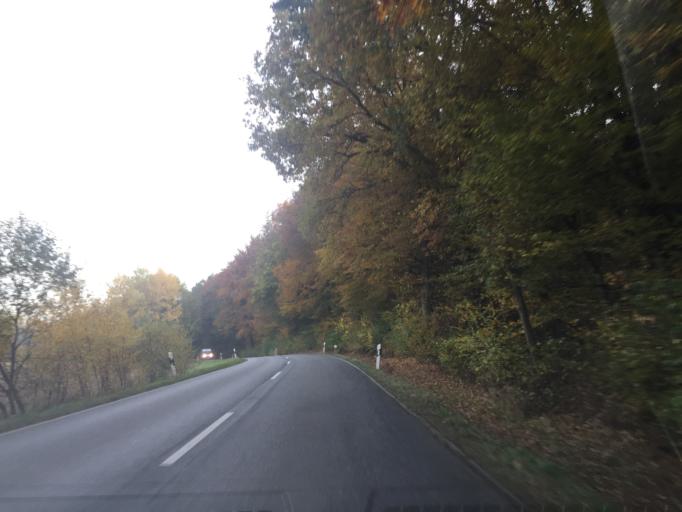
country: DE
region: Rheinland-Pfalz
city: Niedererbach
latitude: 50.4383
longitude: 8.0009
